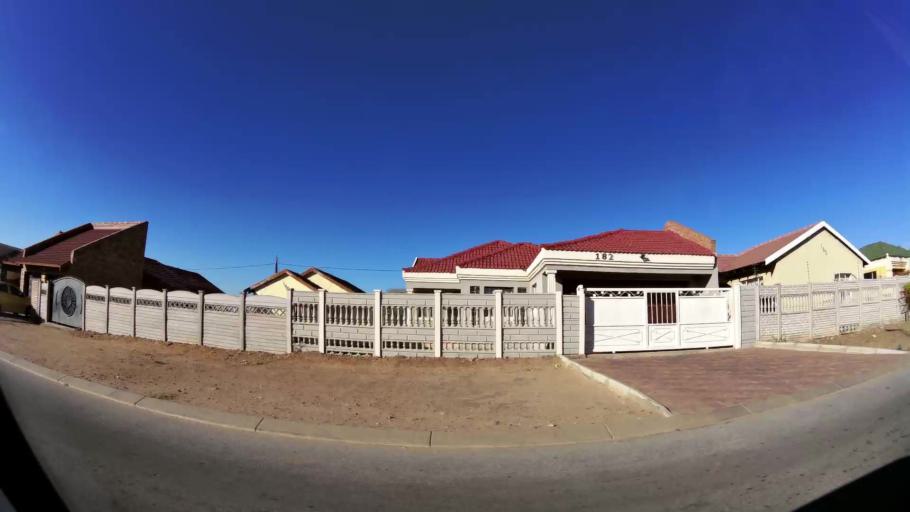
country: ZA
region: Limpopo
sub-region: Capricorn District Municipality
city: Polokwane
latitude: -23.8818
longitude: 29.4737
